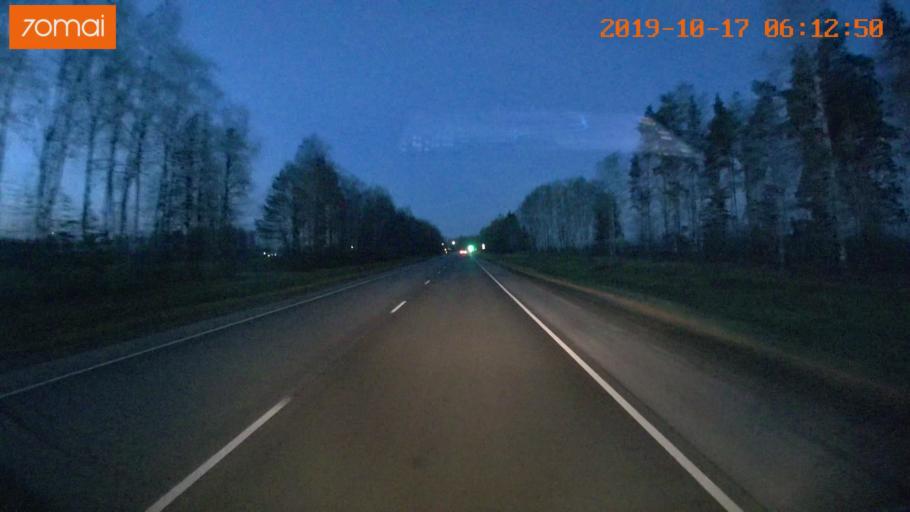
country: RU
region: Ivanovo
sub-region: Gorod Ivanovo
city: Ivanovo
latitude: 56.9056
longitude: 40.9421
